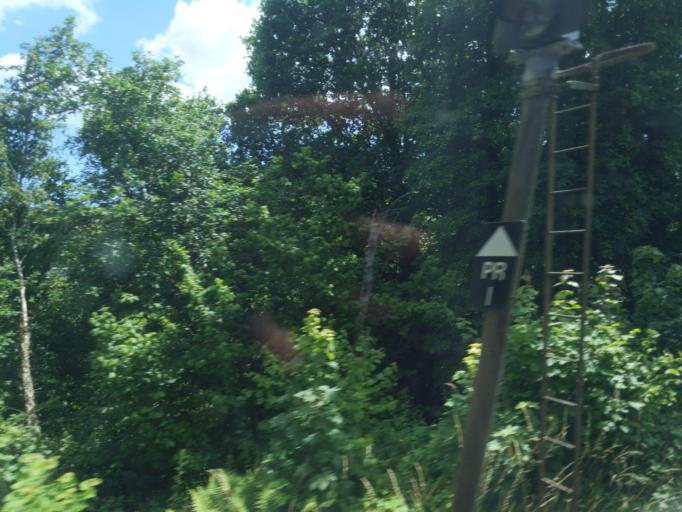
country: GB
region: England
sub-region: Cornwall
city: Par
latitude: 50.3672
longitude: -4.6852
